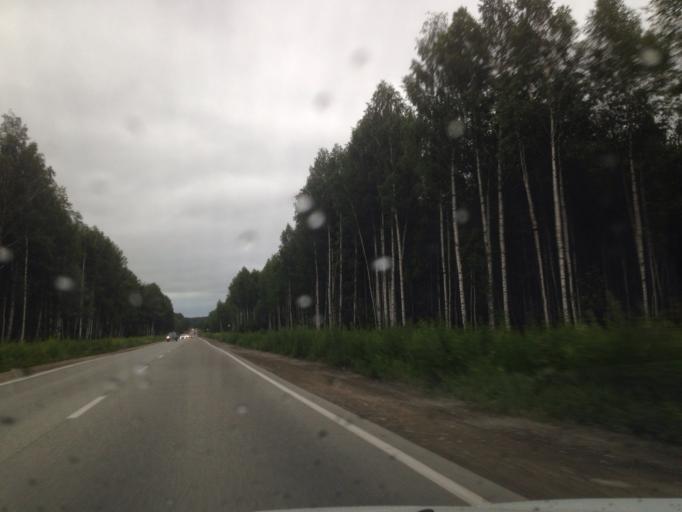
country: RU
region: Sverdlovsk
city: Istok
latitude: 56.8427
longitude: 60.7374
